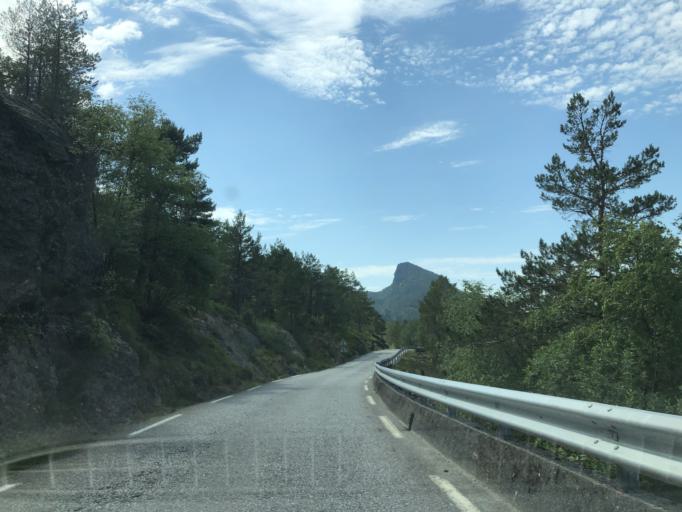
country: NO
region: Hordaland
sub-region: Jondal
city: Jondal
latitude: 60.3133
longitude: 6.3089
